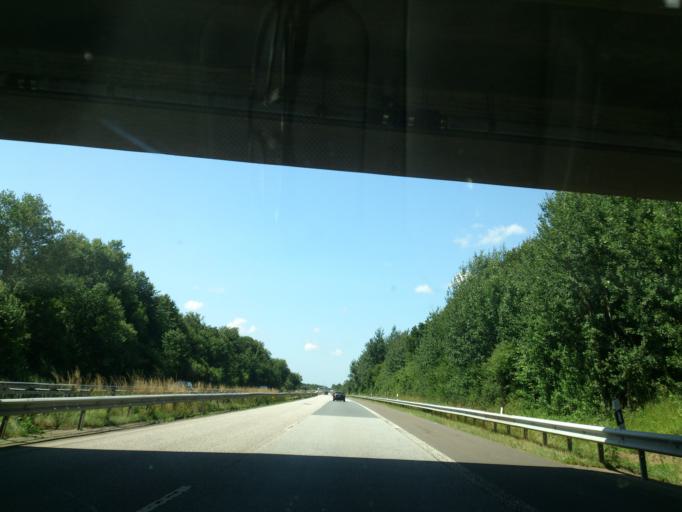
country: DE
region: Schleswig-Holstein
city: Nordhastedt
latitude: 54.1639
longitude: 9.1942
